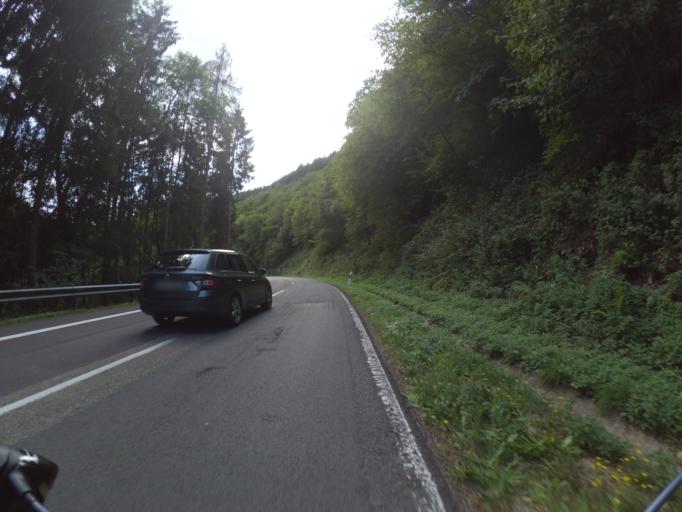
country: DE
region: Rheinland-Pfalz
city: Budlich
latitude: 49.7972
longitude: 6.8988
